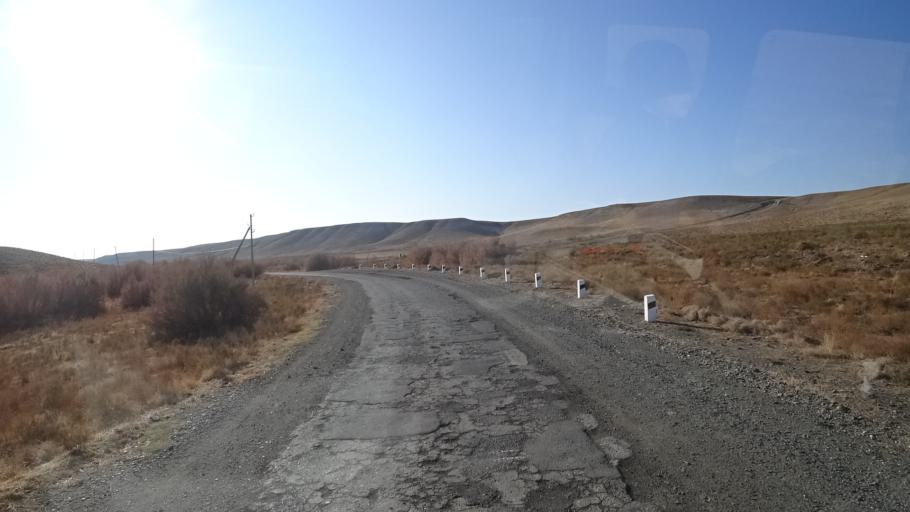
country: UZ
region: Navoiy
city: Beshrabot
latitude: 40.2571
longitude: 65.4439
